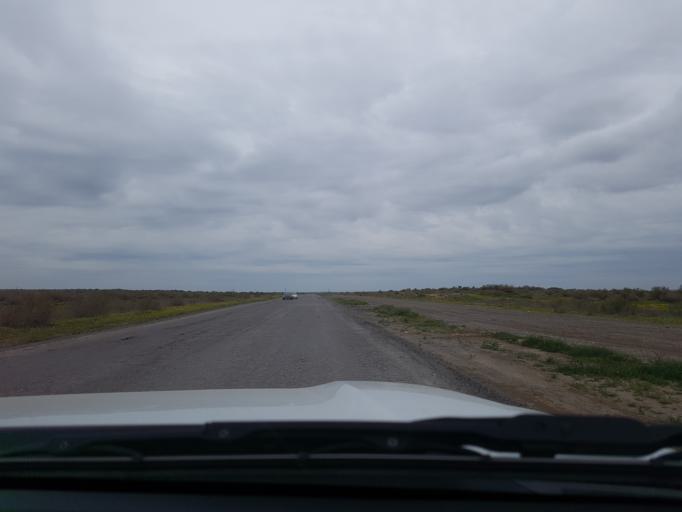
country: TM
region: Mary
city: Bayramaly
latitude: 37.9582
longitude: 62.6551
